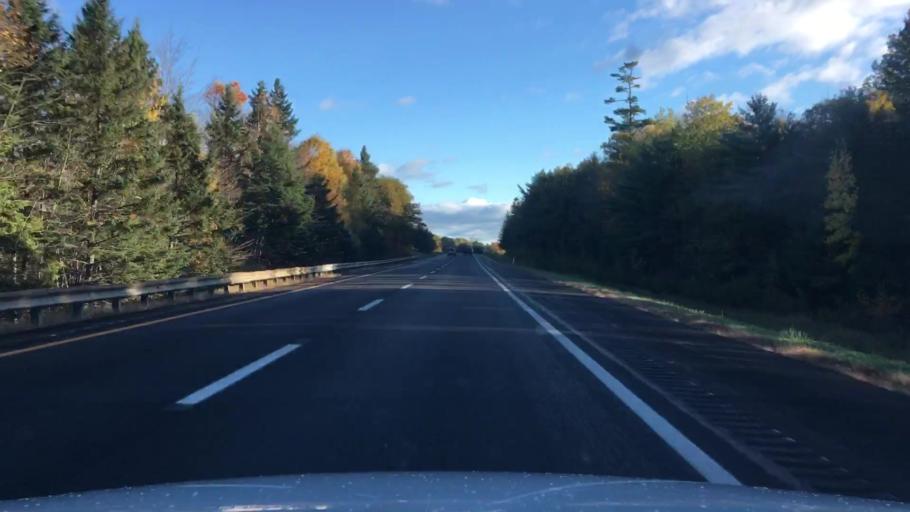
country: US
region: Maine
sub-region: Penobscot County
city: Veazie
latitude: 44.8535
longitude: -68.7242
